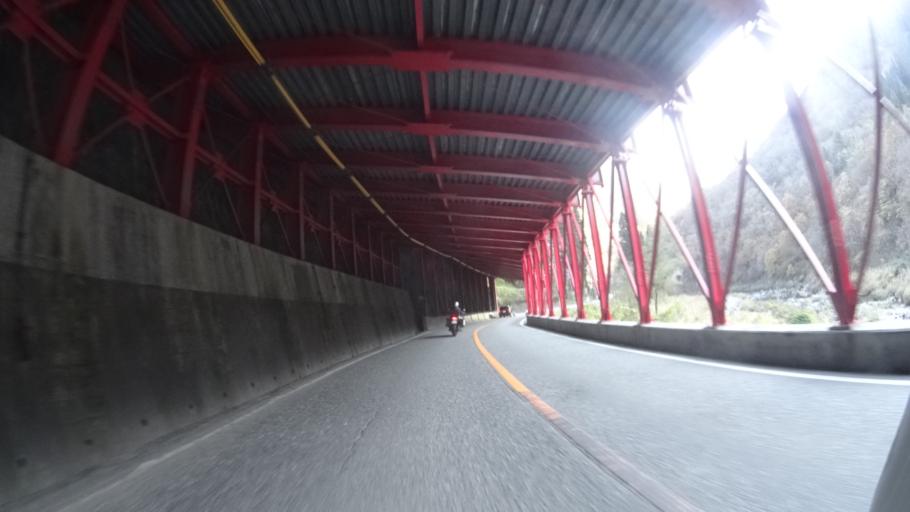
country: JP
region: Fukui
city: Ono
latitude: 35.9087
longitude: 136.6328
